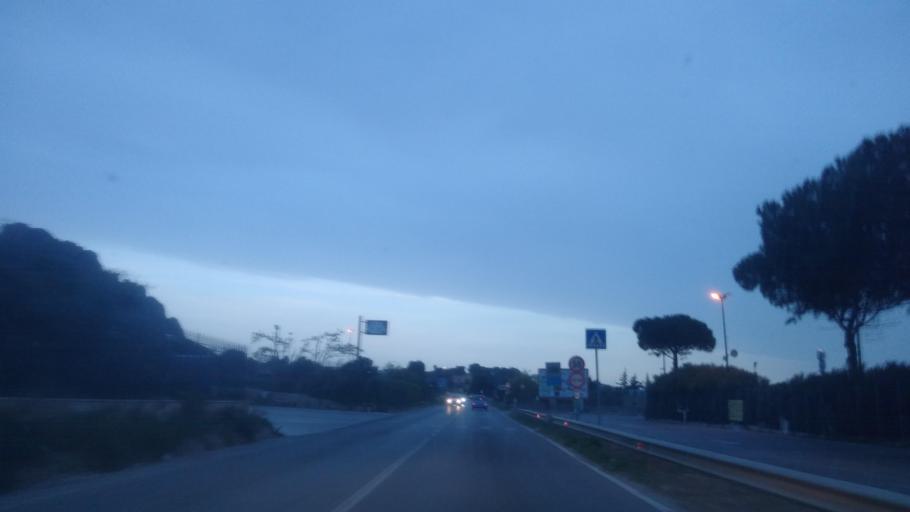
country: IT
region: Sicily
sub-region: Palermo
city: Terrasini
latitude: 38.1409
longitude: 13.0827
